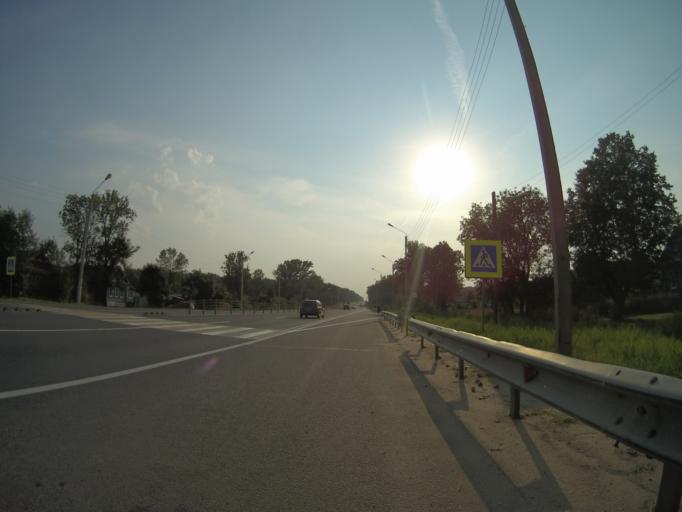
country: RU
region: Vladimir
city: Melekhovo
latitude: 56.2102
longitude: 41.2805
